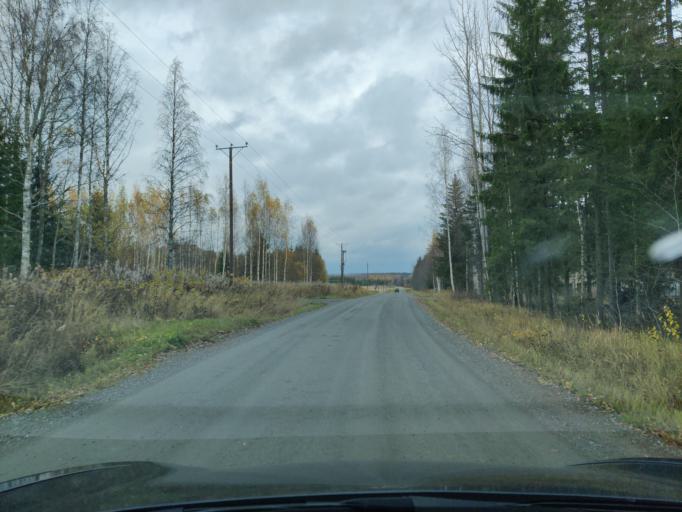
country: FI
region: Northern Savo
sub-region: Kuopio
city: Siilinjaervi
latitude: 63.1179
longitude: 27.5447
